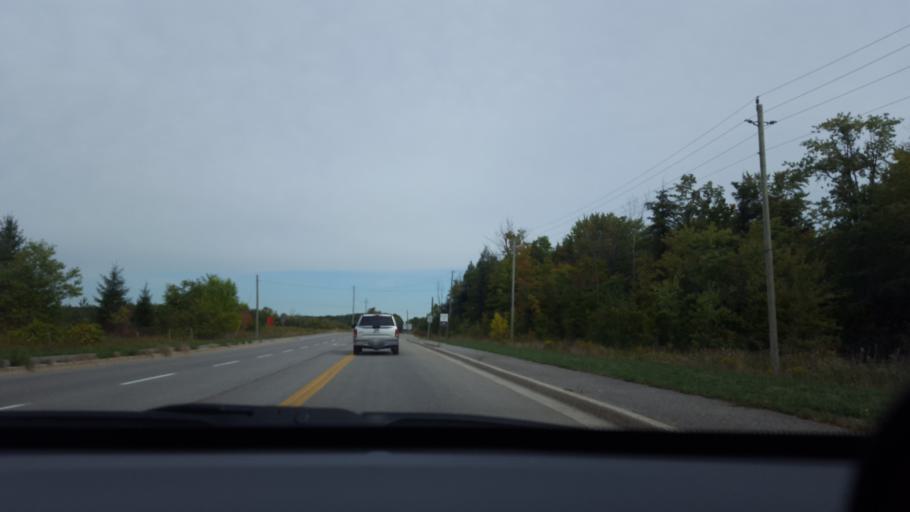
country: CA
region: Ontario
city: Vaughan
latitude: 43.9472
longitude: -79.5332
